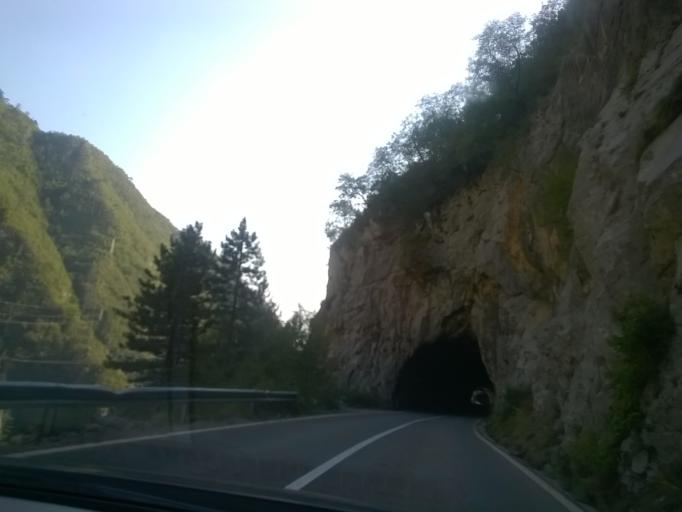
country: ME
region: Opstina Pluzine
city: Pluzine
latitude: 43.2766
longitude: 18.8453
